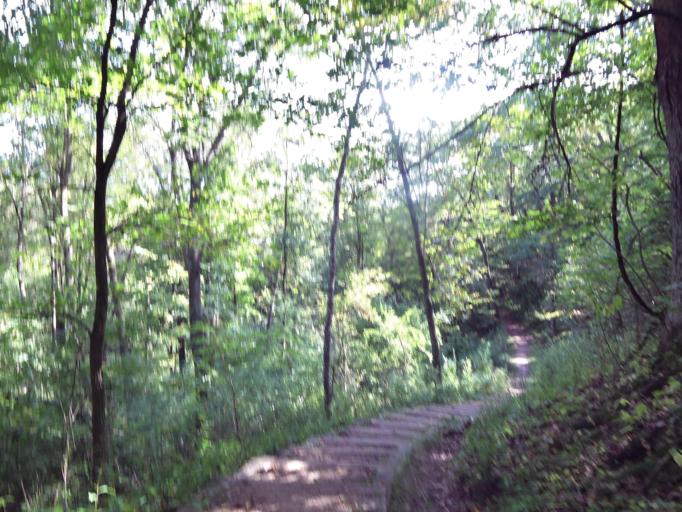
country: US
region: Minnesota
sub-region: Washington County
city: Afton
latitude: 44.8585
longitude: -92.7933
